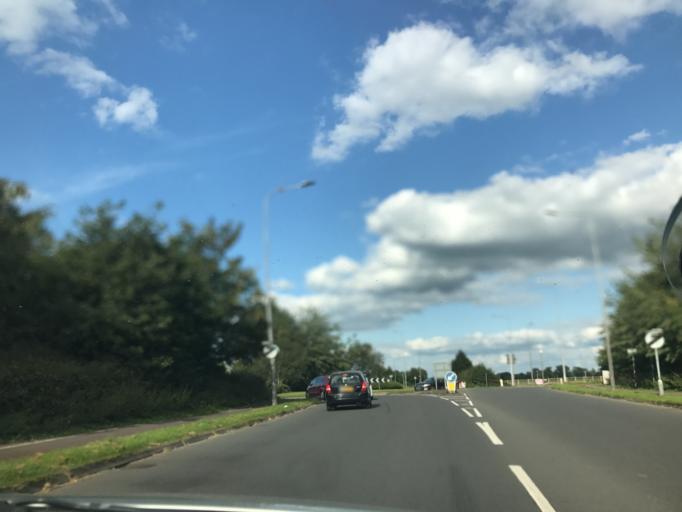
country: GB
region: England
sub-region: Cheshire East
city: Nantwich
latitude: 53.0785
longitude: -2.5110
